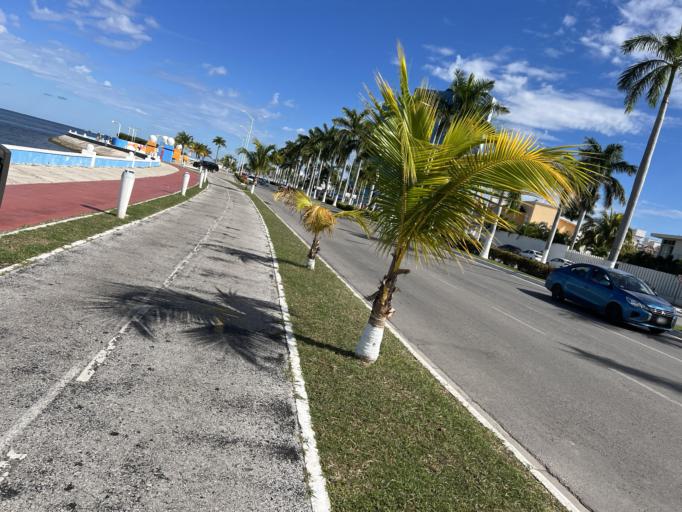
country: MX
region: Campeche
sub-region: Campeche
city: Campeche
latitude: 19.8434
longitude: -90.5443
